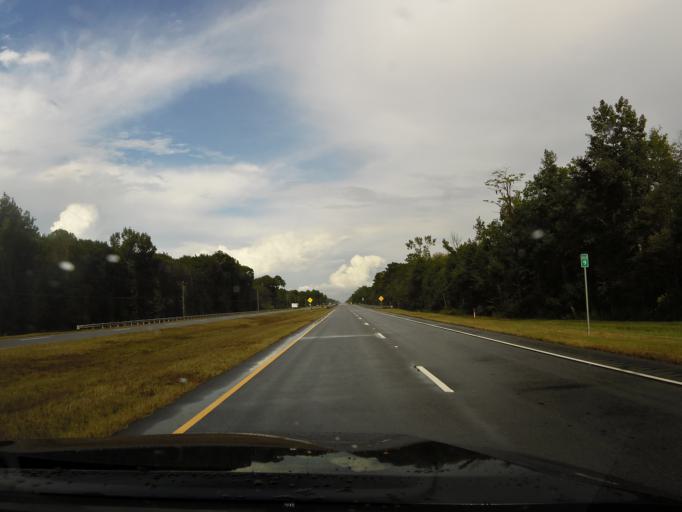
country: US
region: Georgia
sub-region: Long County
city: Ludowici
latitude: 31.7338
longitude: -81.7071
